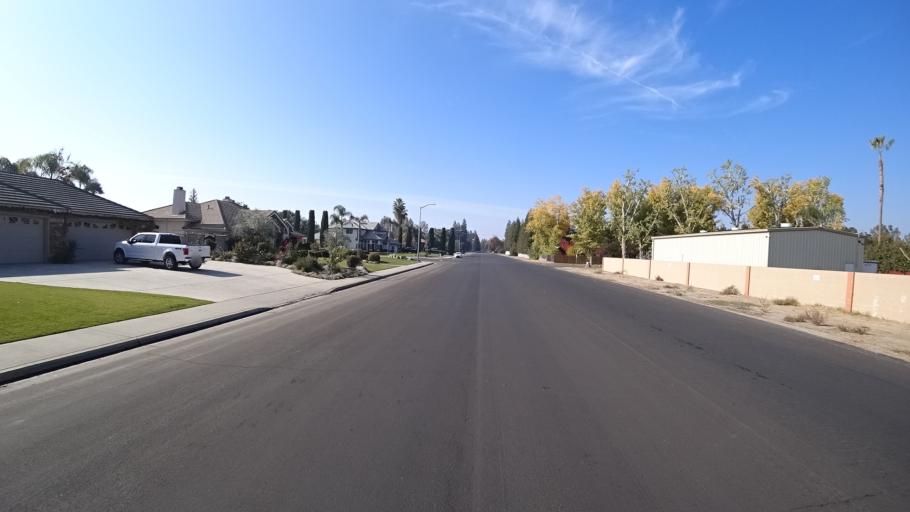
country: US
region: California
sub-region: Kern County
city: Rosedale
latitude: 35.3617
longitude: -119.1780
